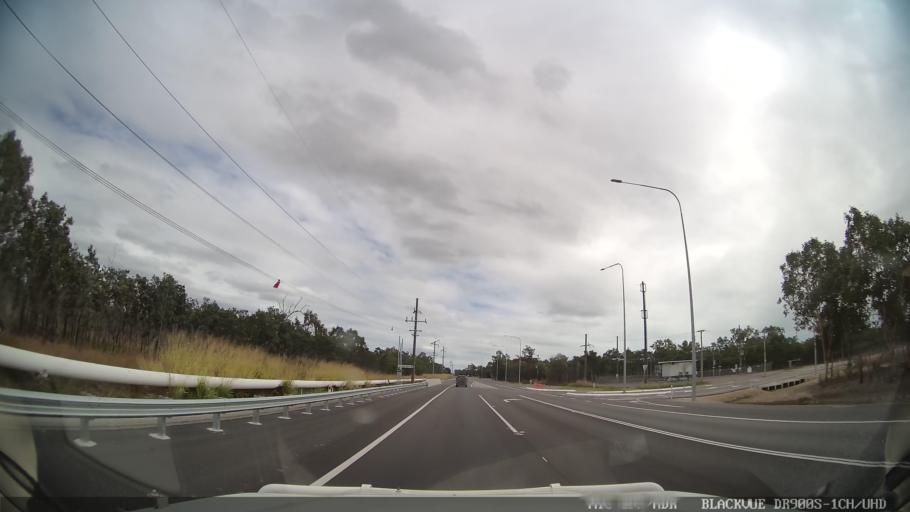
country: AU
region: Queensland
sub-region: Townsville
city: Bohle Plains
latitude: -19.1811
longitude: 146.5591
